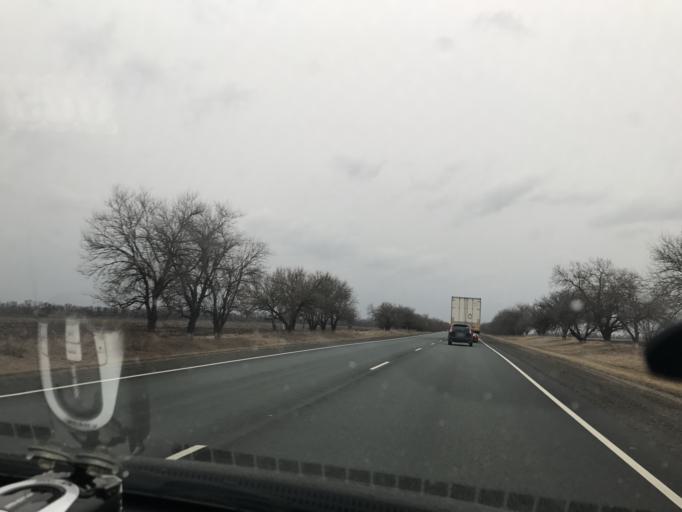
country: RU
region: Krasnodarskiy
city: Novoleushkovskaya
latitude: 46.0509
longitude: 39.9607
